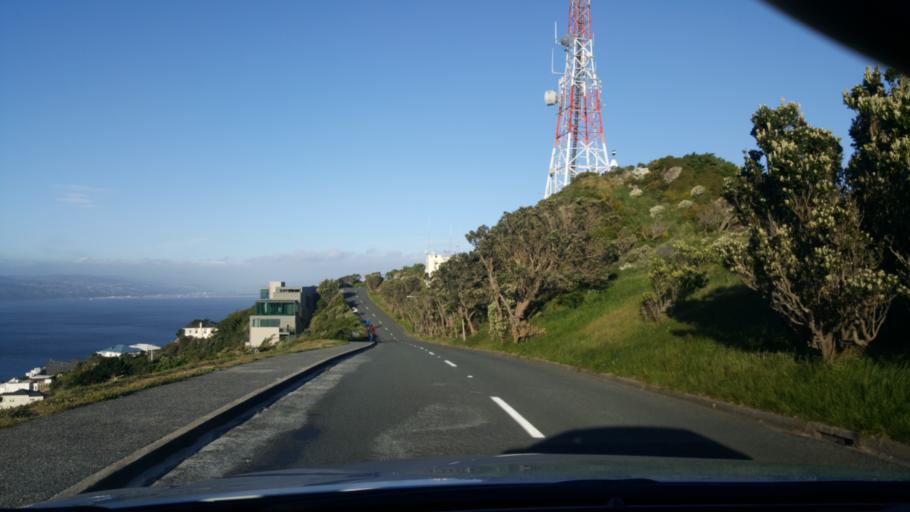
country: NZ
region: Wellington
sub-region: Wellington City
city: Wellington
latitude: -41.2963
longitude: 174.7955
